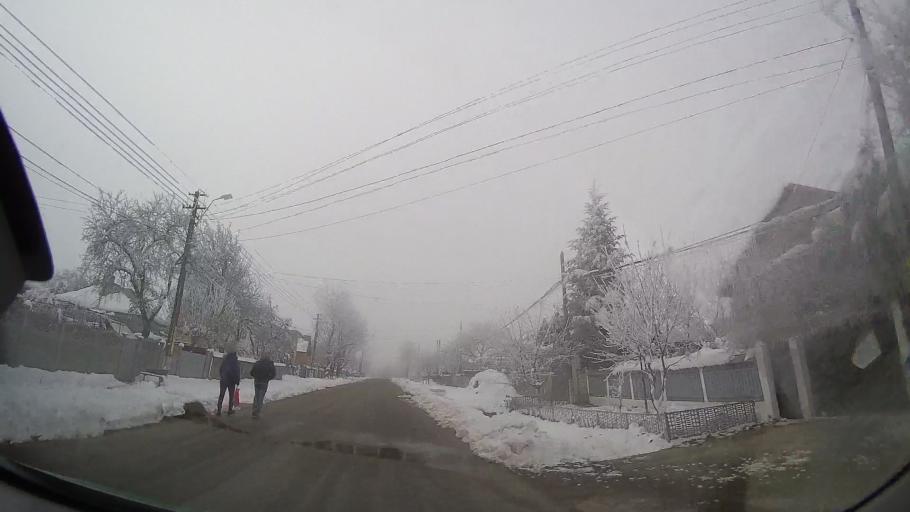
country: RO
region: Iasi
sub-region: Comuna Valea Seaca
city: Valea Seaca
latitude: 47.2939
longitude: 26.6712
